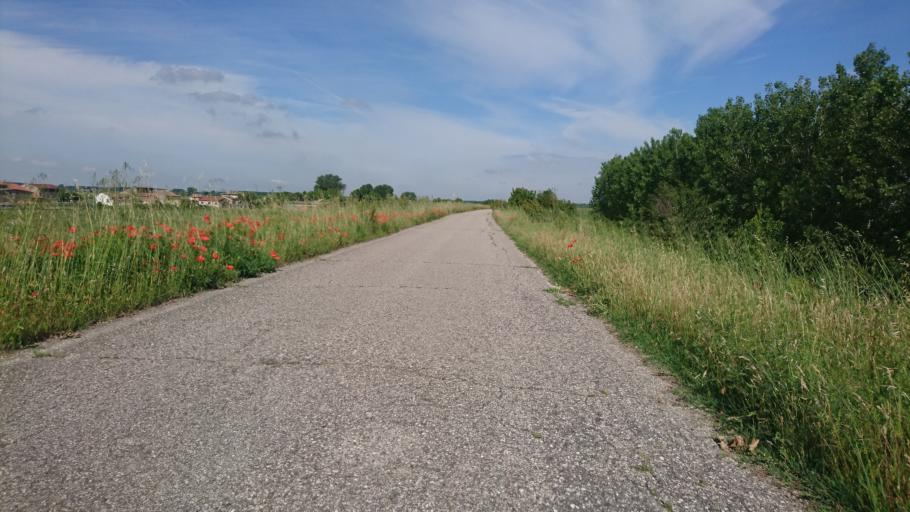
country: IT
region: Lombardy
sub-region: Provincia di Mantova
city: Carbonara di Po
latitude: 45.0397
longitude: 11.2238
